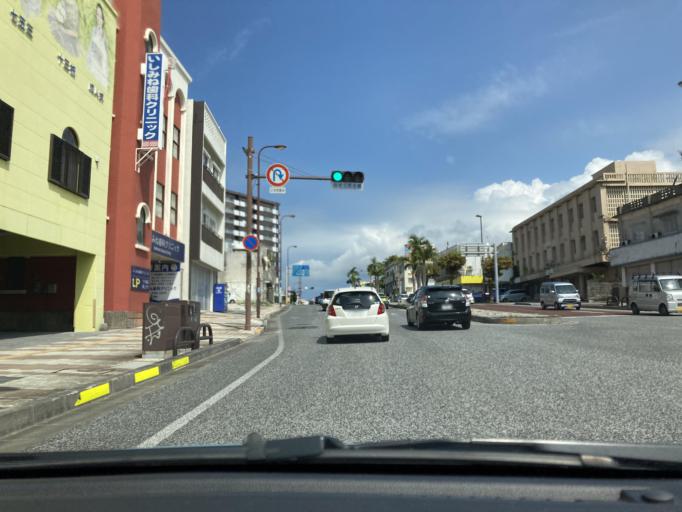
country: JP
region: Okinawa
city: Okinawa
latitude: 26.3222
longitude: 127.7932
